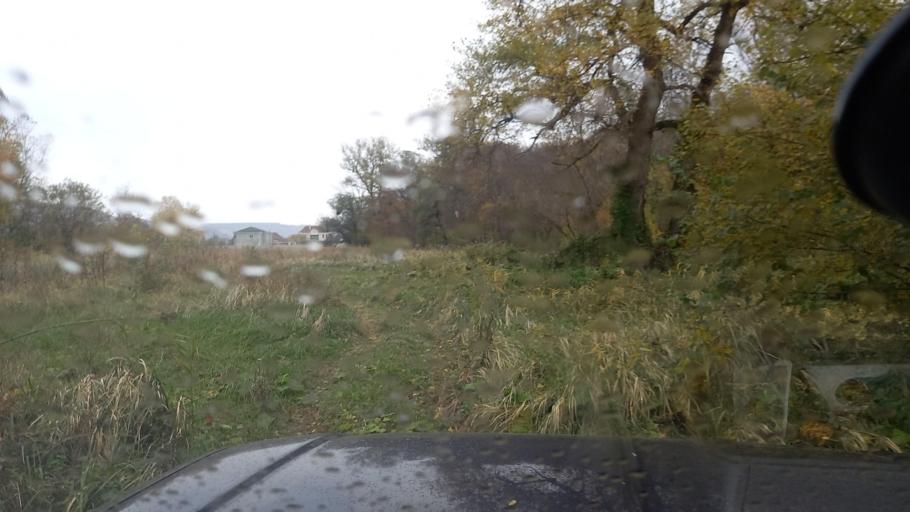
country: RU
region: Krasnodarskiy
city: Shedok
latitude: 44.1717
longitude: 40.8448
